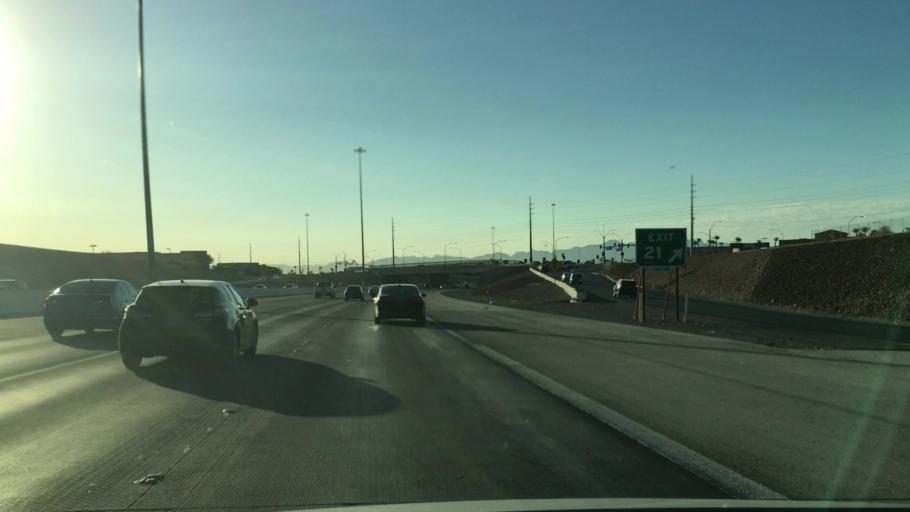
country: US
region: Nevada
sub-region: Clark County
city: Summerlin South
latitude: 36.1170
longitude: -115.3067
